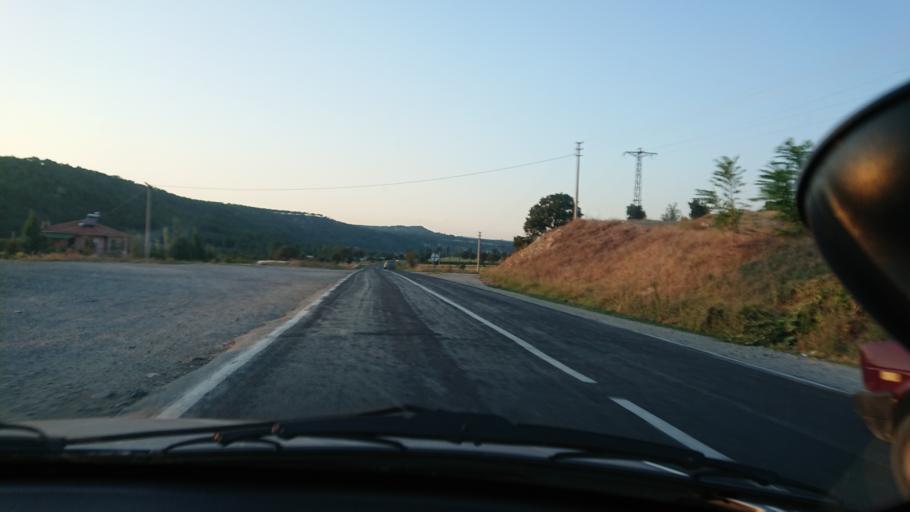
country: TR
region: Usak
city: Gure
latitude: 38.7455
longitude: 29.1999
